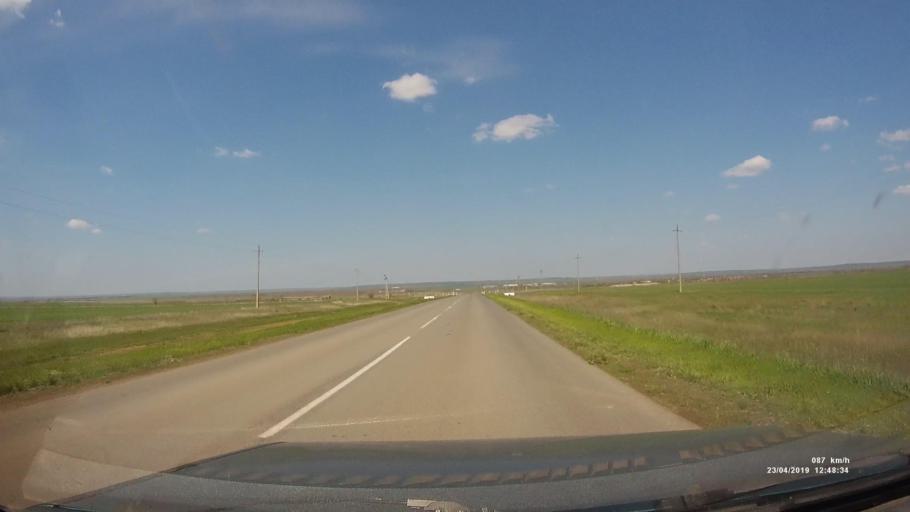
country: RU
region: Kalmykiya
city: Yashalta
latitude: 46.5263
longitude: 42.6388
